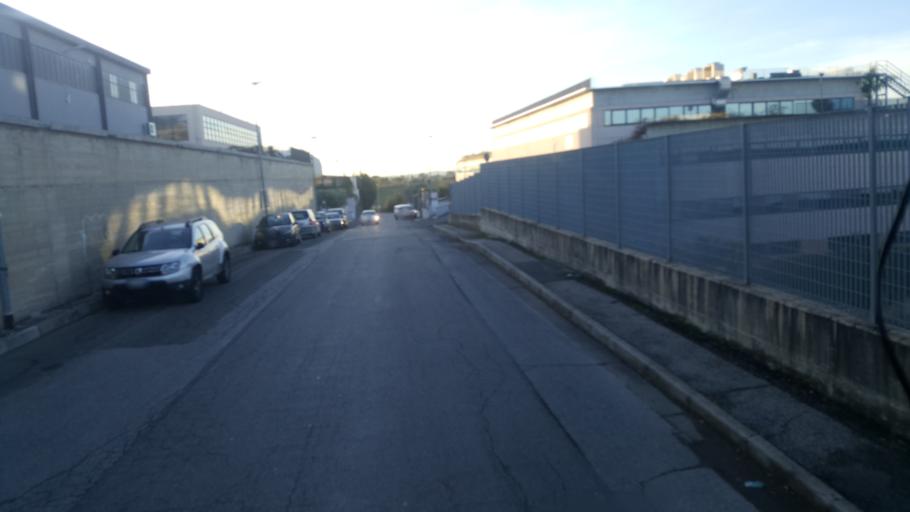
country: IT
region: Latium
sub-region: Citta metropolitana di Roma Capitale
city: Formello
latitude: 42.0512
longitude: 12.4029
